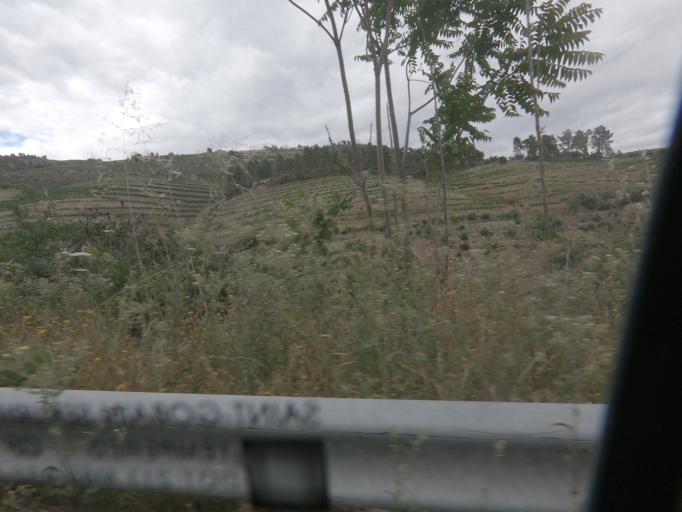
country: PT
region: Vila Real
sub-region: Sabrosa
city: Vilela
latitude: 41.1976
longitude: -7.5525
